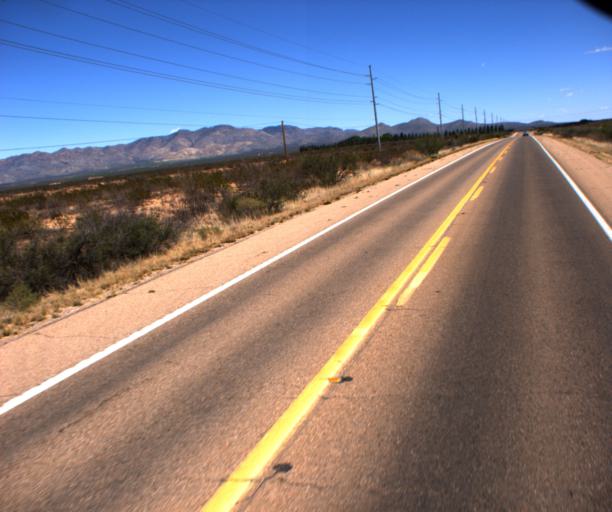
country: US
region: Arizona
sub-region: Cochise County
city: Sierra Vista Southeast
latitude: 31.3800
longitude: -110.0937
